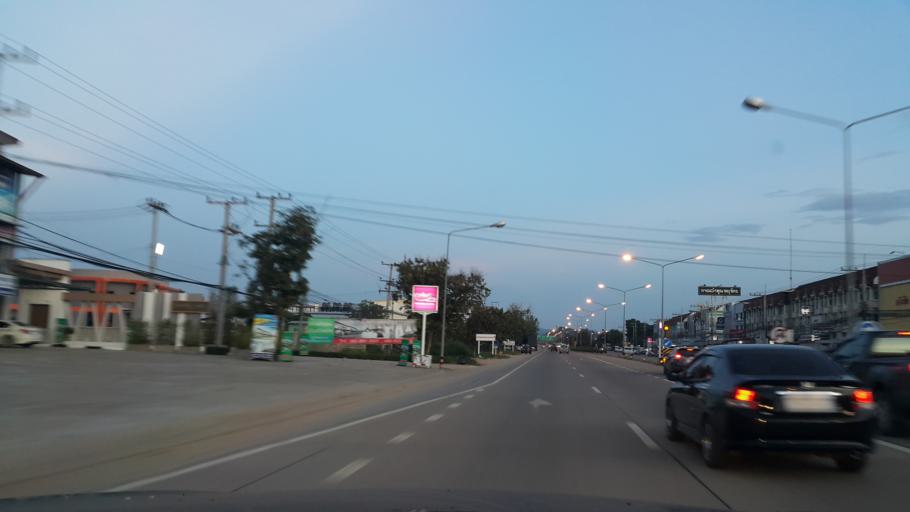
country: TH
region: Lamphun
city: Lamphun
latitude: 18.5607
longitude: 99.0358
